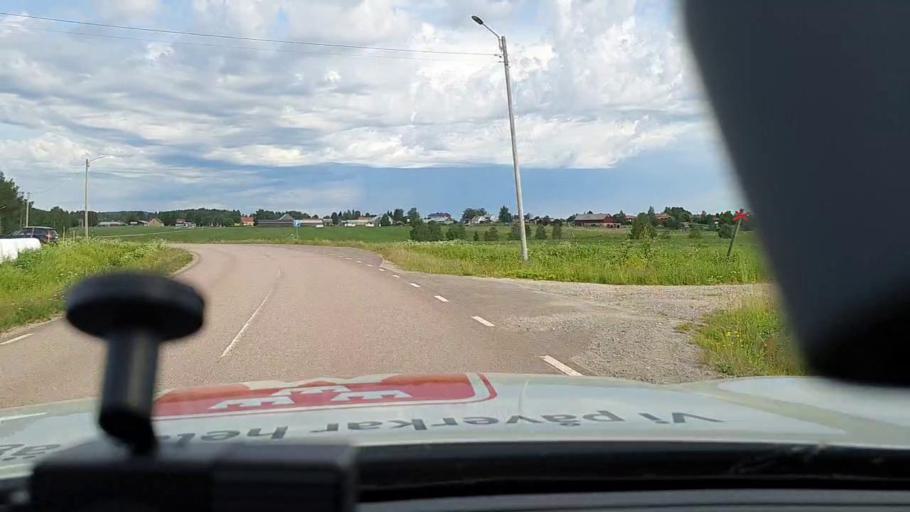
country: SE
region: Norrbotten
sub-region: Bodens Kommun
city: Saevast
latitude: 65.7042
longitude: 21.7682
